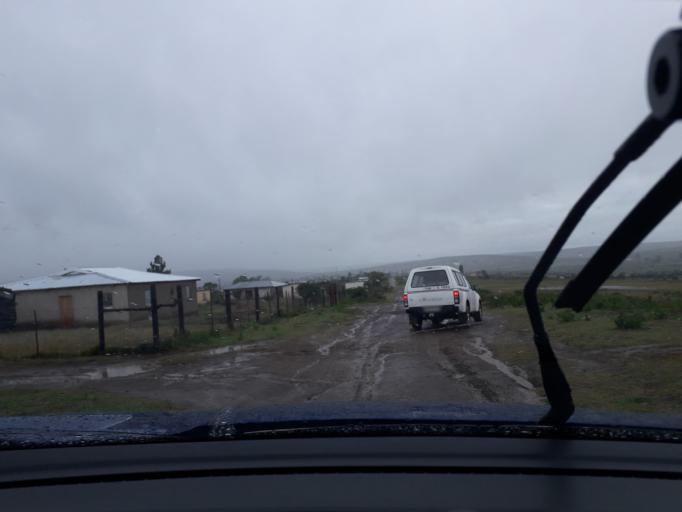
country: ZA
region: Eastern Cape
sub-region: Buffalo City Metropolitan Municipality
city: Bhisho
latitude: -32.8070
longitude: 27.3639
